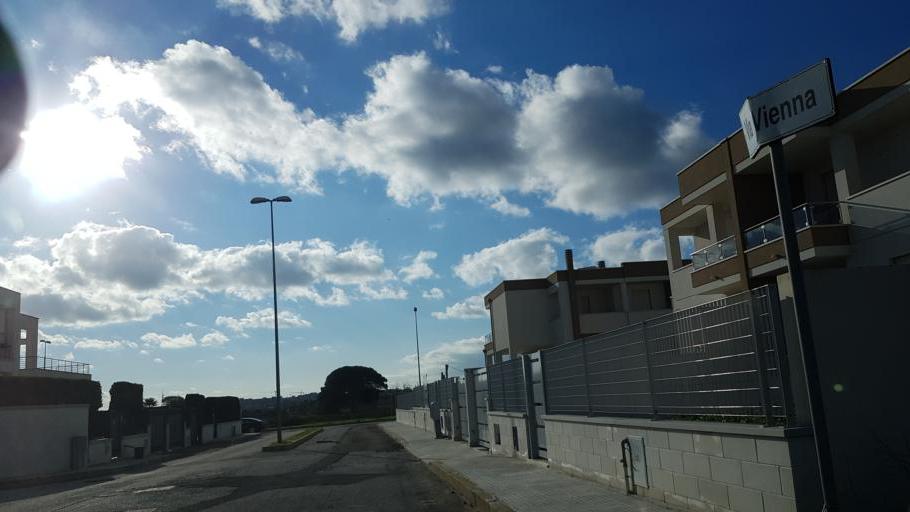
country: IT
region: Apulia
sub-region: Provincia di Brindisi
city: Brindisi
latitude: 40.6421
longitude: 17.9173
